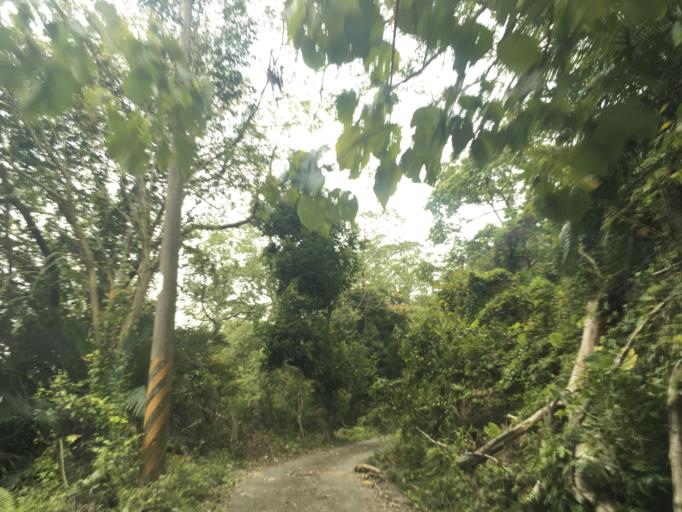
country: TW
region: Taiwan
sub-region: Taichung City
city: Taichung
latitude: 24.1354
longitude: 120.8225
